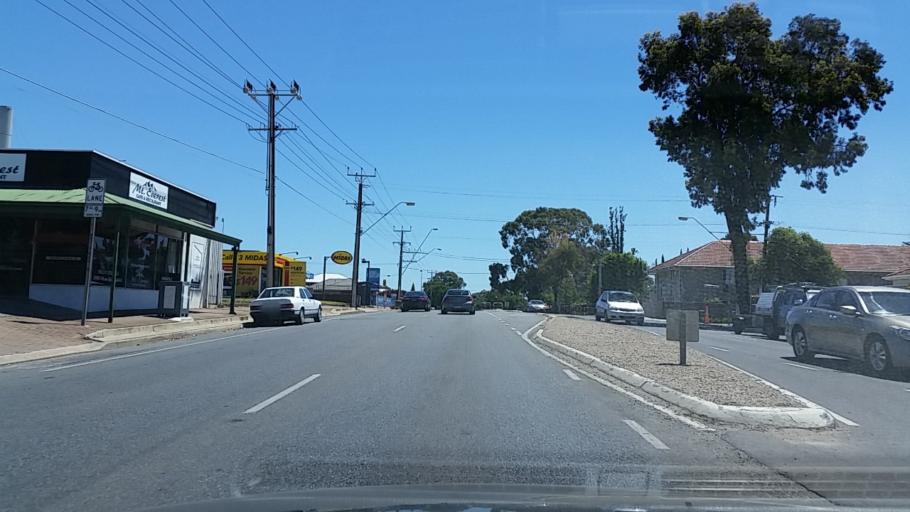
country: AU
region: South Australia
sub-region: Norwood Payneham St Peters
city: Payneham
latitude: -34.8924
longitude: 138.6491
